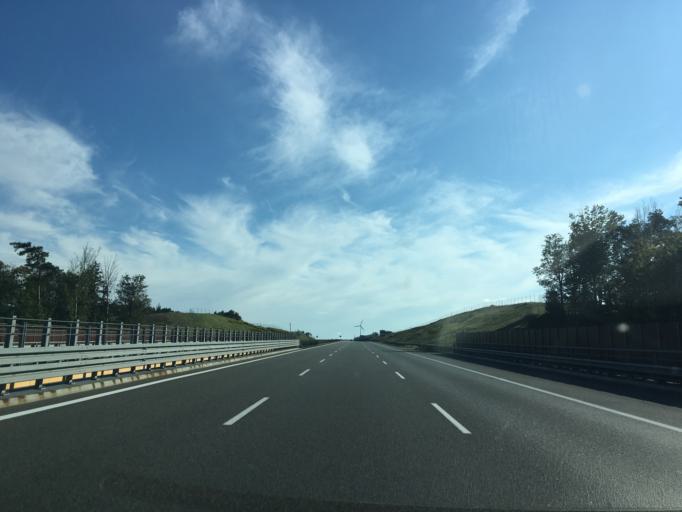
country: PL
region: Kujawsko-Pomorskie
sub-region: Powiat chelminski
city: Lisewo
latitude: 53.3922
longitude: 18.6853
